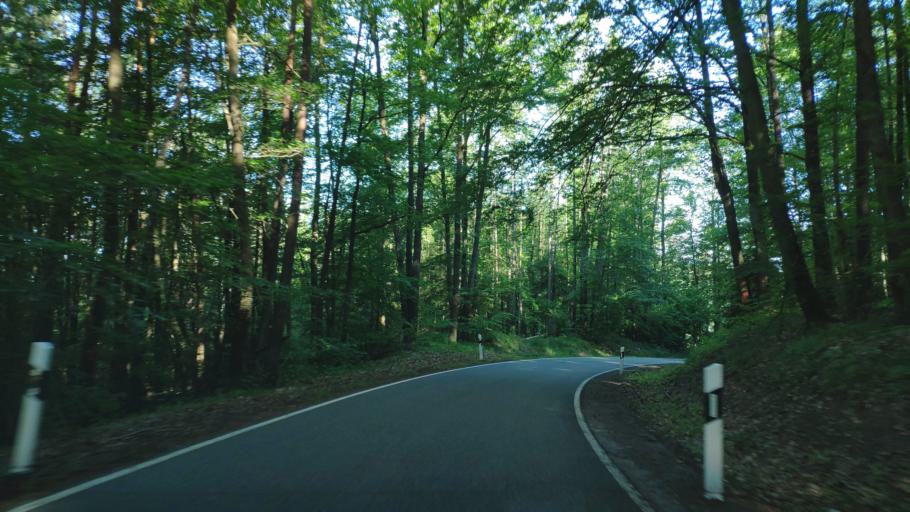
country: DE
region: Rheinland-Pfalz
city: Rumbach
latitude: 49.0851
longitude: 7.7942
